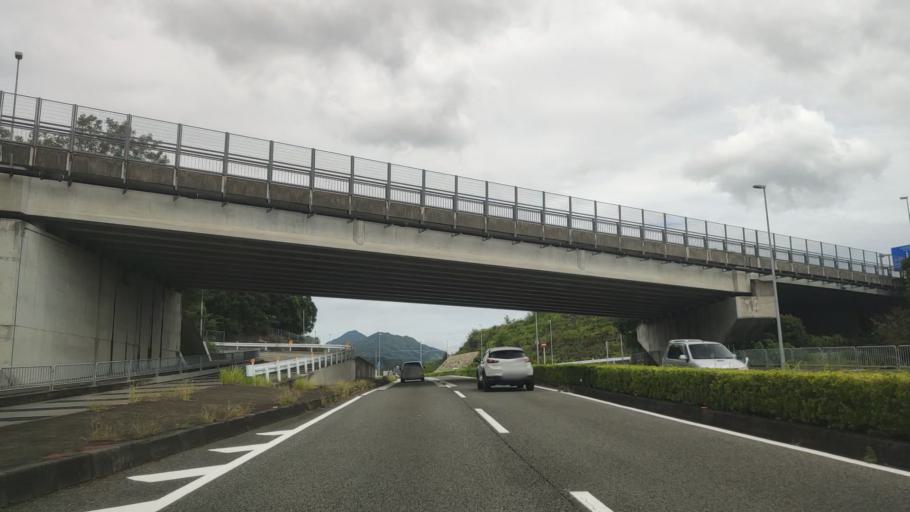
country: JP
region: Wakayama
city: Tanabe
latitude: 33.7321
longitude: 135.4005
